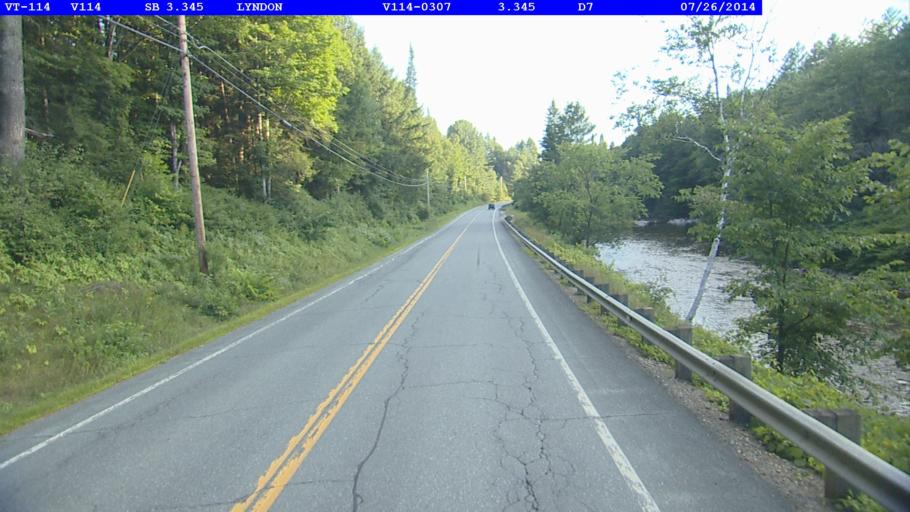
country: US
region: Vermont
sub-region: Caledonia County
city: Lyndonville
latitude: 44.5731
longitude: -71.9507
